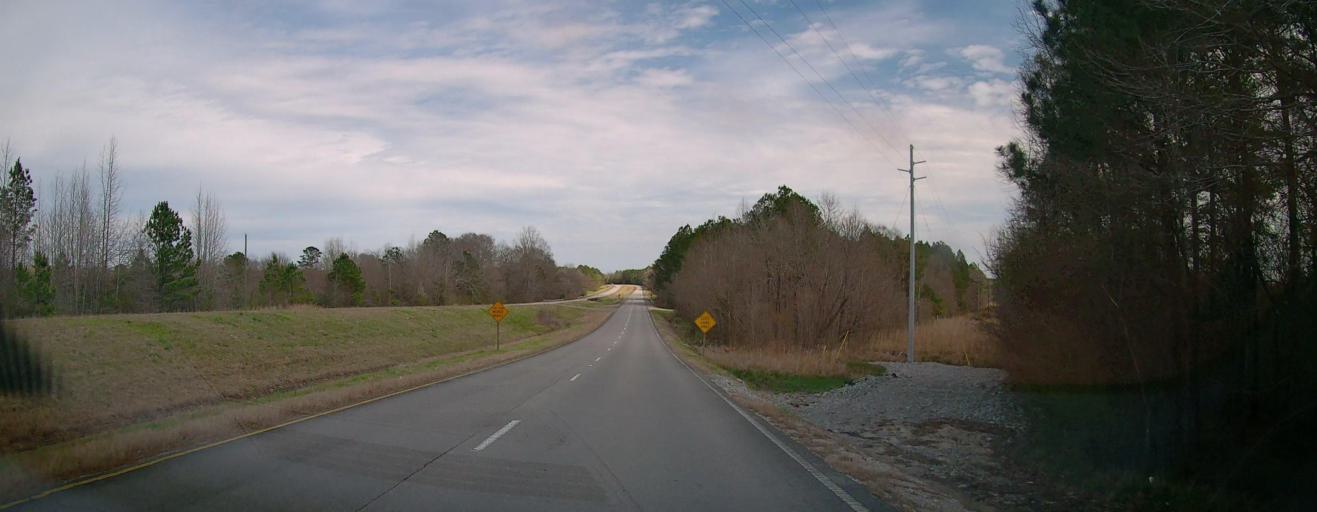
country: US
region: Alabama
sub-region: Marion County
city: Winfield
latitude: 33.9300
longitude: -87.6836
